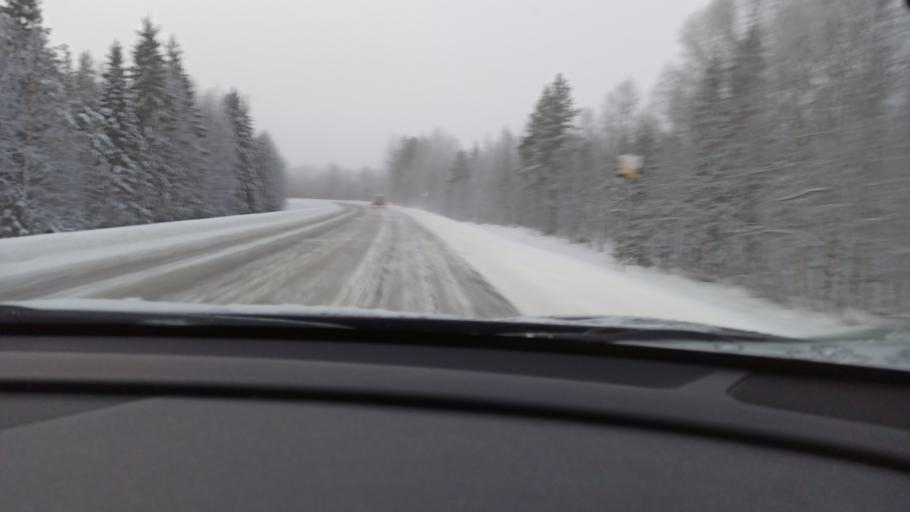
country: FI
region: Lapland
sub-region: Pohjois-Lappi
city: Sodankylae
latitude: 66.9255
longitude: 26.2088
